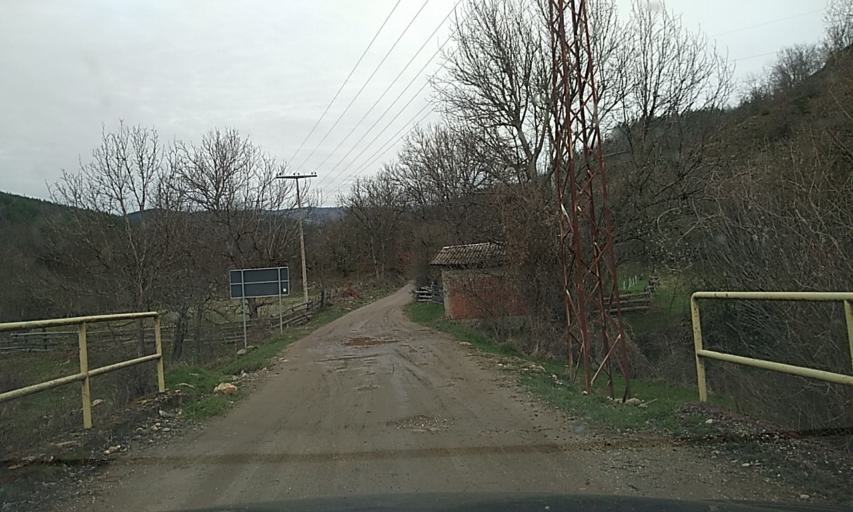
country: RS
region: Central Serbia
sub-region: Pcinjski Okrug
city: Bosilegrad
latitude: 42.3577
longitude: 22.4175
